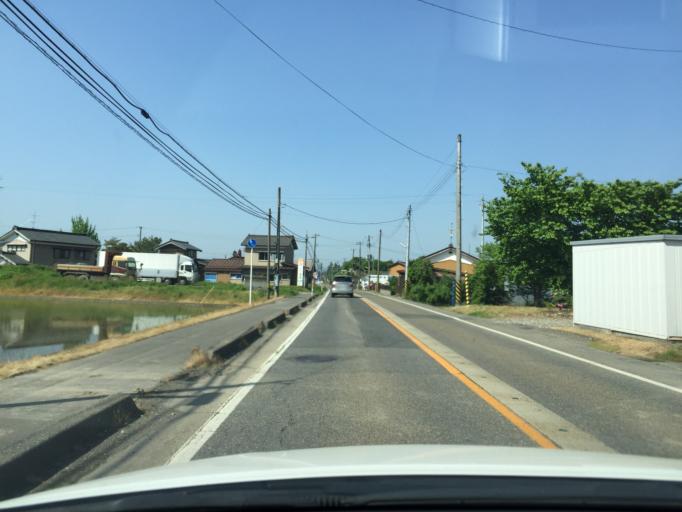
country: JP
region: Niigata
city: Muramatsu
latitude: 37.7033
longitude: 139.1952
